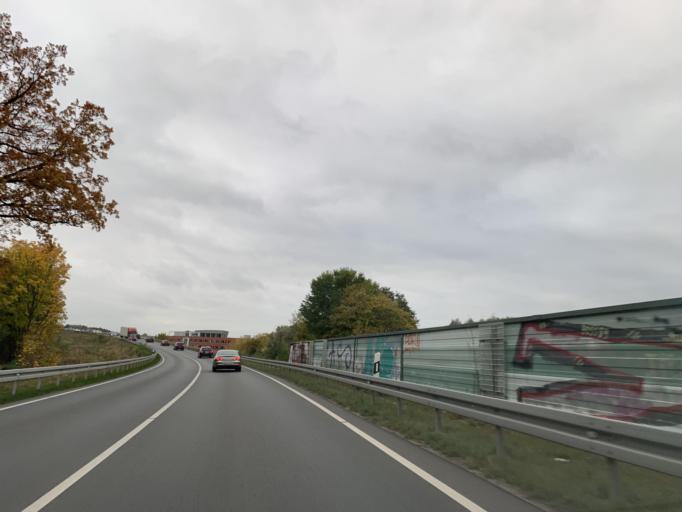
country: DE
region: Mecklenburg-Vorpommern
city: Neubrandenburg
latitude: 53.5526
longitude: 13.2768
